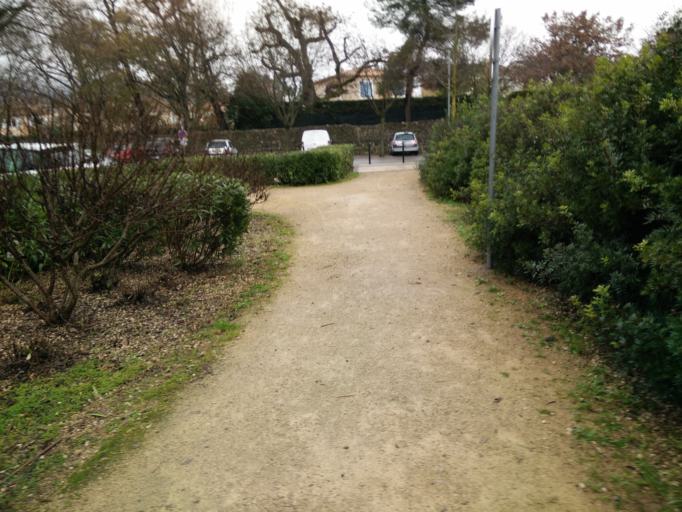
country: FR
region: Provence-Alpes-Cote d'Azur
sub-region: Departement des Alpes-Maritimes
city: Mouans-Sartoux
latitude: 43.6167
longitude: 6.9707
